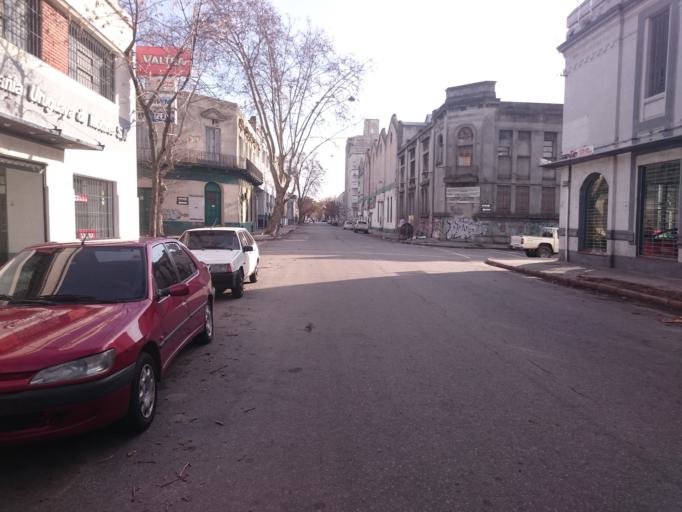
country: UY
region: Montevideo
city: Montevideo
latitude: -34.8971
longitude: -56.1911
